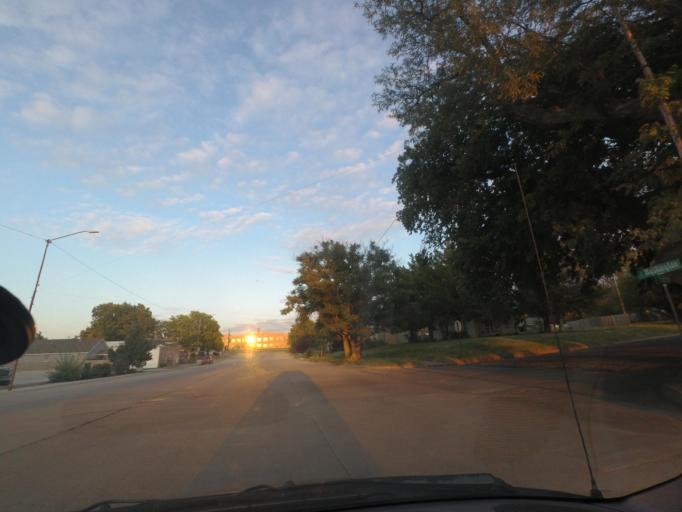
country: US
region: Kansas
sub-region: Cheyenne County
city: Saint Francis
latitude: 39.7742
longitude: -101.7979
